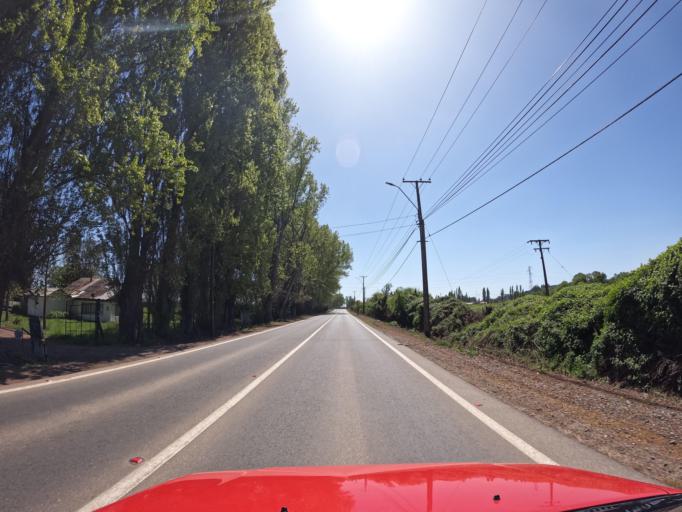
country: CL
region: Maule
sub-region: Provincia de Linares
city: Colbun
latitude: -35.7476
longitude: -71.4201
